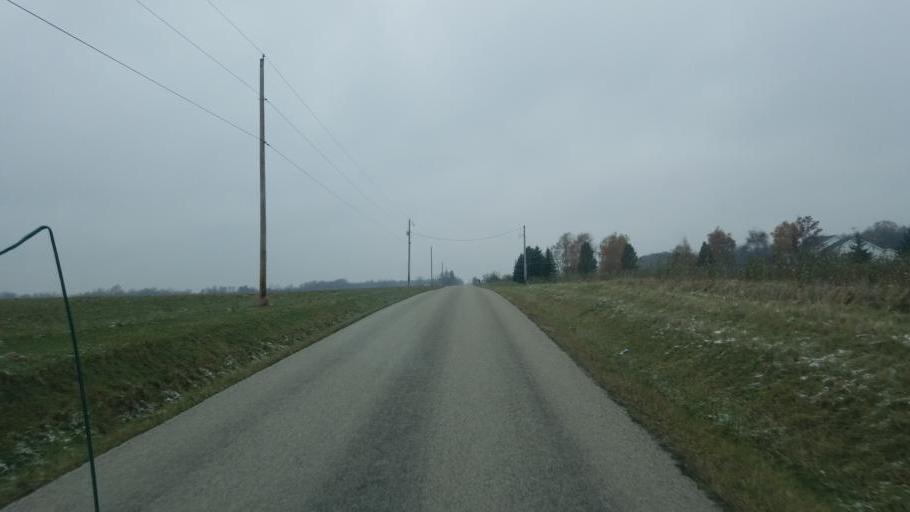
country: US
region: Ohio
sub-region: Huron County
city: New London
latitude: 41.0168
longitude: -82.3256
